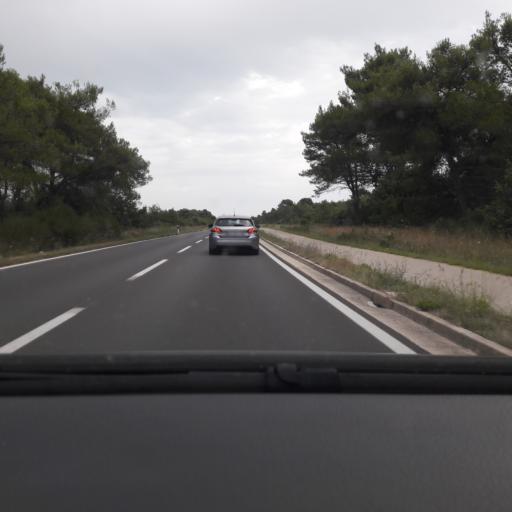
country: HR
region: Zadarska
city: Nin
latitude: 44.1812
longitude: 15.1872
